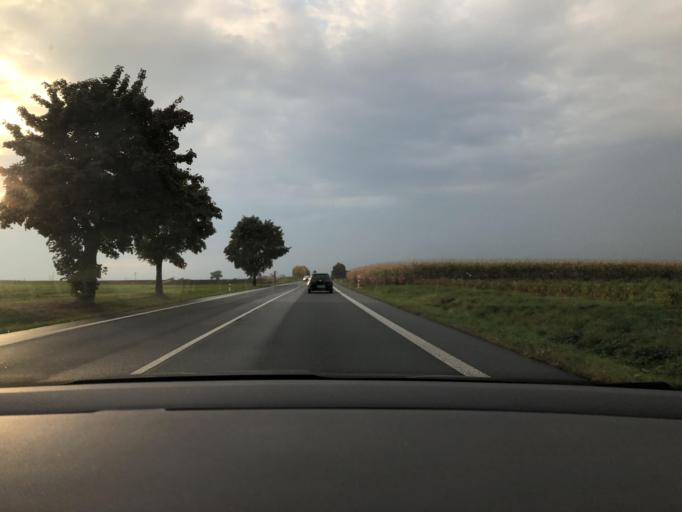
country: CZ
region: Central Bohemia
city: Velim
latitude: 50.0383
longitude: 15.1190
